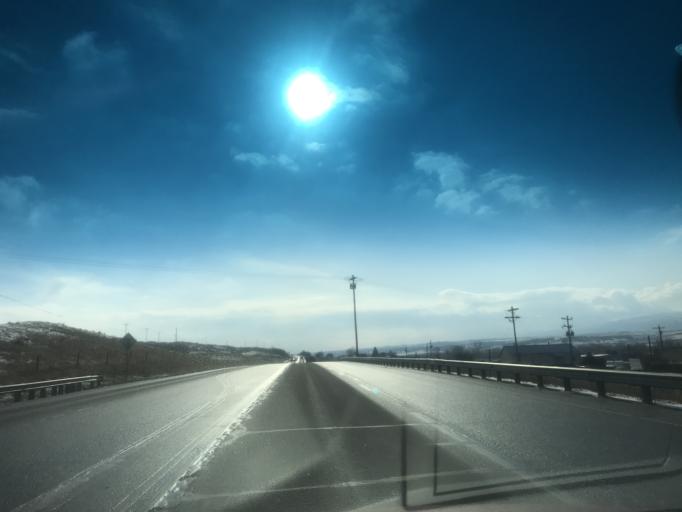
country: US
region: Colorado
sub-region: Douglas County
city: Highlands Ranch
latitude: 39.4701
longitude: -104.9885
